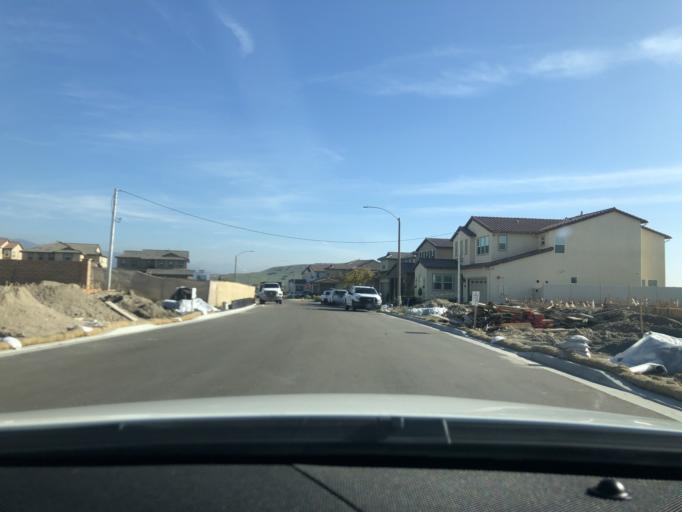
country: US
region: California
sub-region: San Diego County
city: Bonita
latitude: 32.6070
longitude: -116.9931
